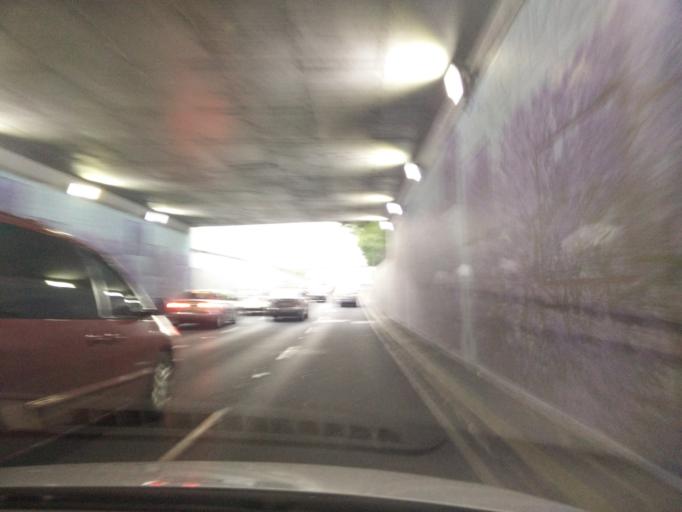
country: MX
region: Mexico City
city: Colonia Nativitas
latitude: 19.4035
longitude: -99.1289
